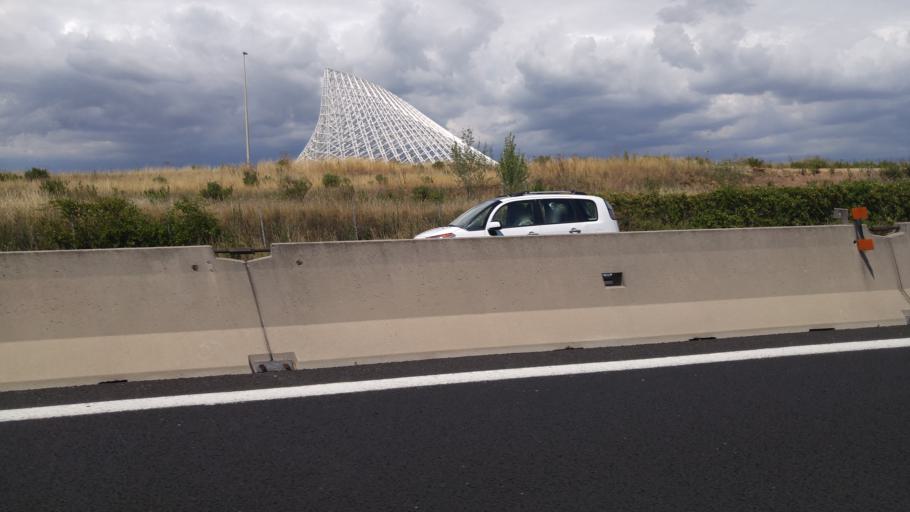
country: IT
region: Latium
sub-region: Citta metropolitana di Roma Capitale
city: Frascati
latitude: 41.8400
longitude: 12.6336
